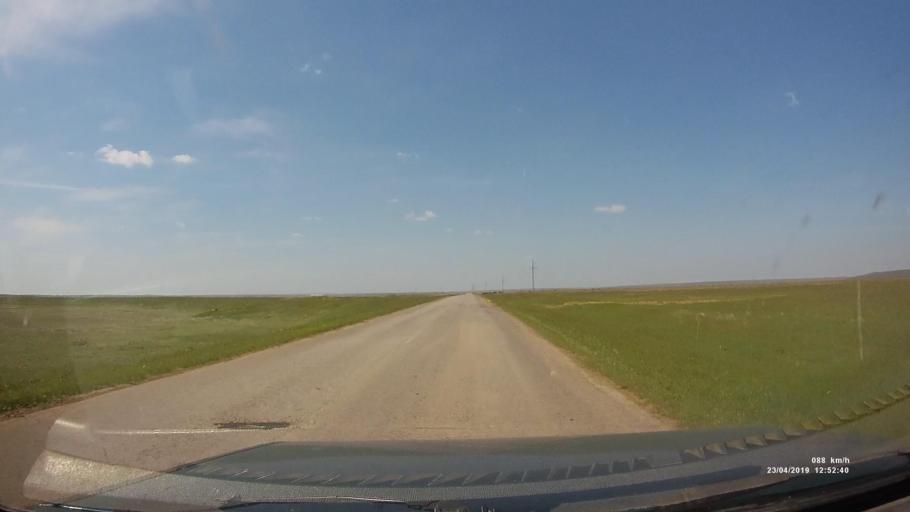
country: RU
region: Kalmykiya
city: Yashalta
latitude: 46.5668
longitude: 42.6066
